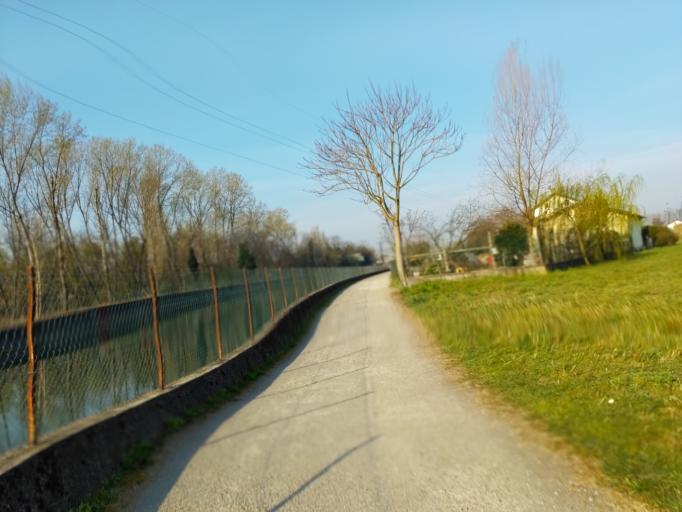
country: IT
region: Piedmont
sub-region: Provincia di Torino
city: San Mauro Torinese
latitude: 45.0943
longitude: 7.7348
